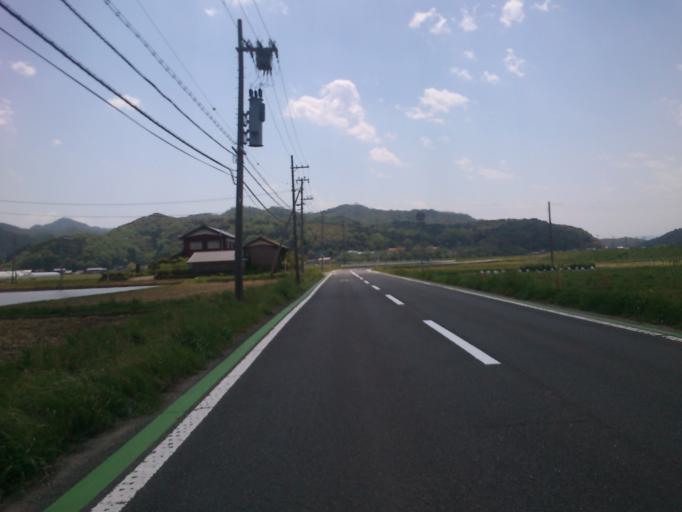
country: JP
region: Kyoto
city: Miyazu
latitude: 35.7199
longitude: 135.1079
